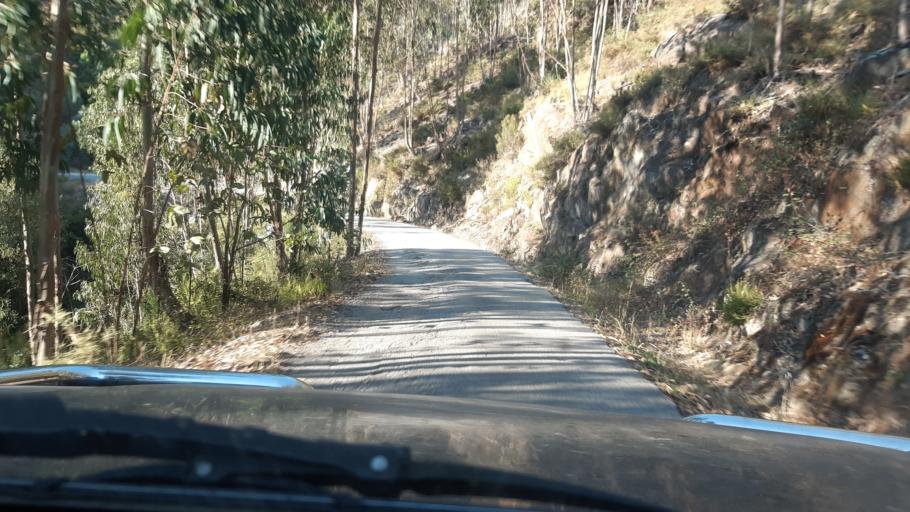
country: PT
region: Viseu
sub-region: Mortagua
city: Mortagua
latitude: 40.5321
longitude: -8.2510
